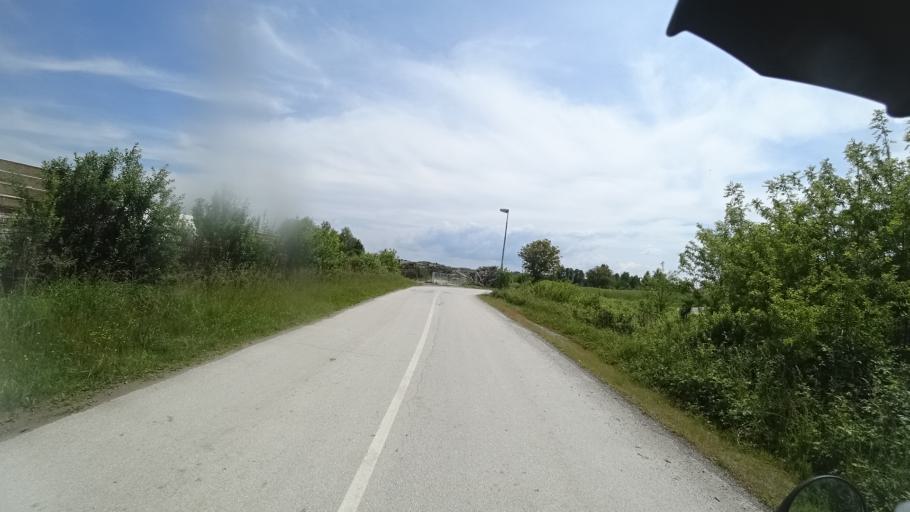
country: HR
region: Sisacko-Moslavacka
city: Gvozd
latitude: 45.3475
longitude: 15.8649
